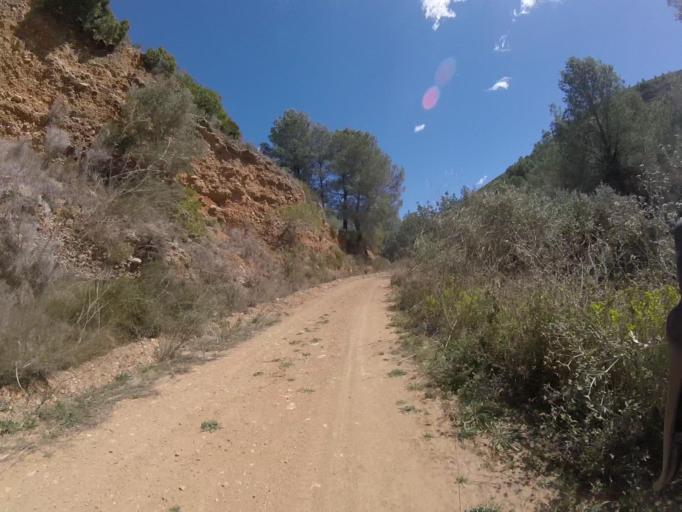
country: ES
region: Valencia
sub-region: Provincia de Castello
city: Orpesa/Oropesa del Mar
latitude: 40.1670
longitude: 0.1265
